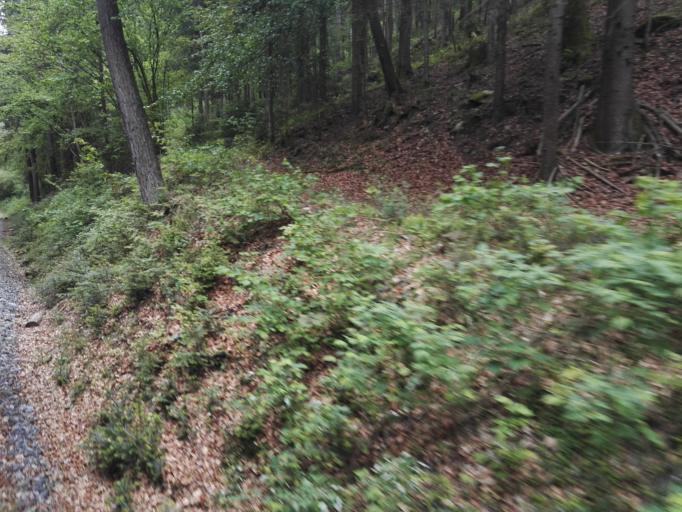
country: AT
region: Styria
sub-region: Politischer Bezirk Weiz
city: Koglhof
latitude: 47.3269
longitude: 15.6957
